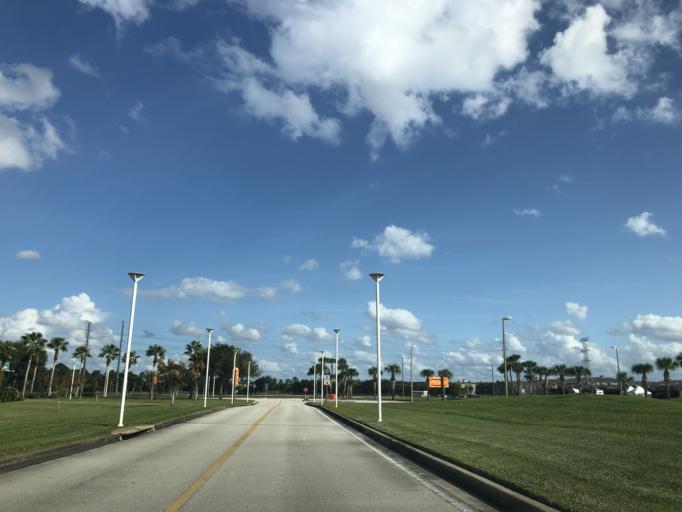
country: US
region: Florida
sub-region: Orange County
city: Williamsburg
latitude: 28.4317
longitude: -81.4569
